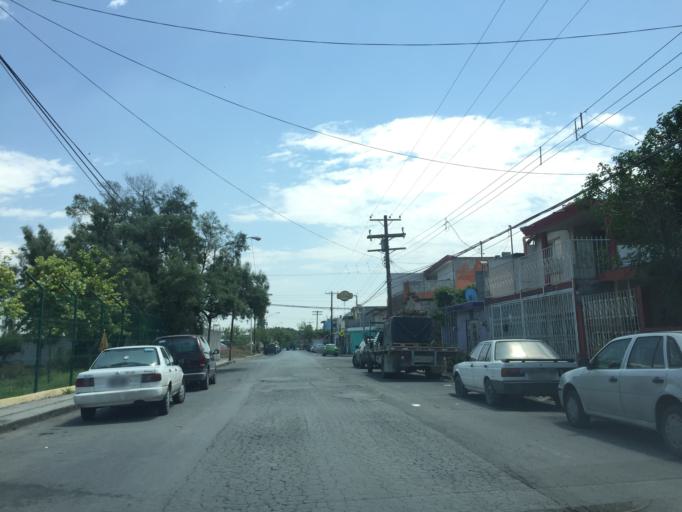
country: MX
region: Nuevo Leon
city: Apodaca
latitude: 25.7806
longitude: -100.1837
